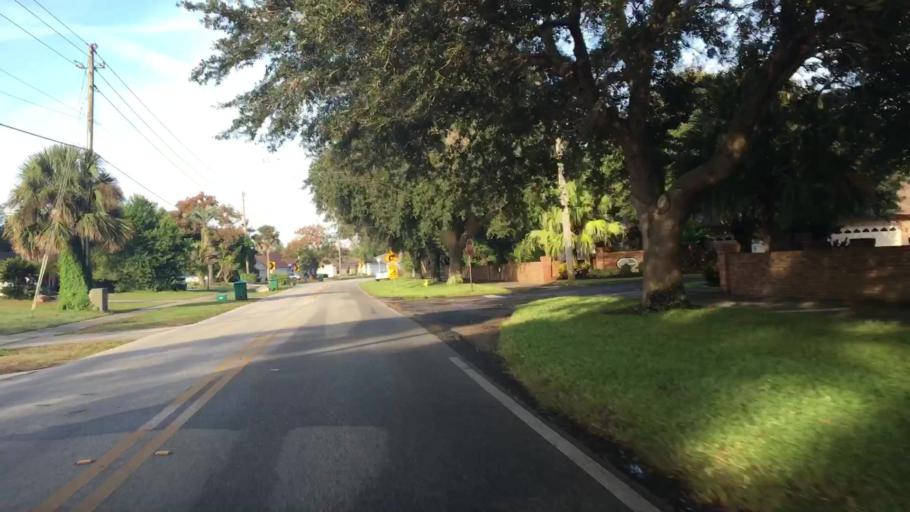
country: US
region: Florida
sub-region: Volusia County
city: Deltona
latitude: 28.9228
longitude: -81.2427
